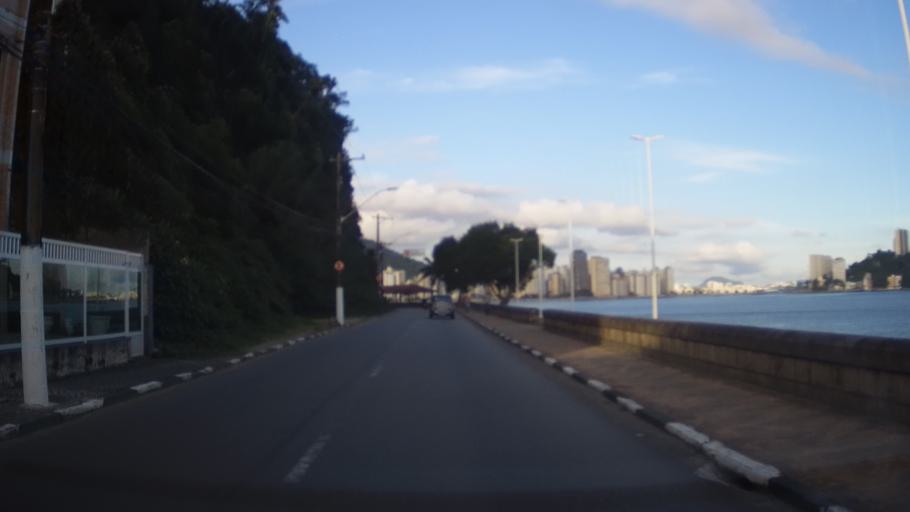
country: BR
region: Sao Paulo
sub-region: Sao Vicente
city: Sao Vicente
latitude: -23.9746
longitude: -46.3870
